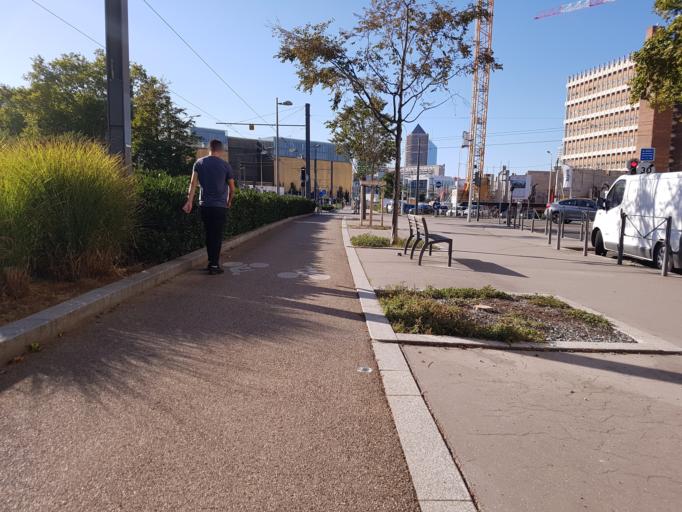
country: FR
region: Rhone-Alpes
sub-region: Departement du Rhone
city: Lyon
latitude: 45.7539
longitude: 4.8642
